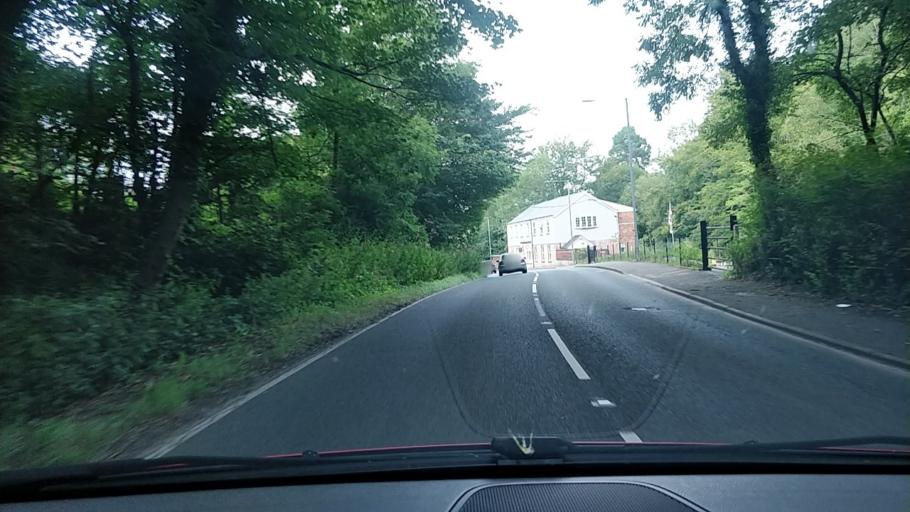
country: GB
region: Wales
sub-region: County of Flintshire
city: Leeswood
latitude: 53.1331
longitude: -3.0819
